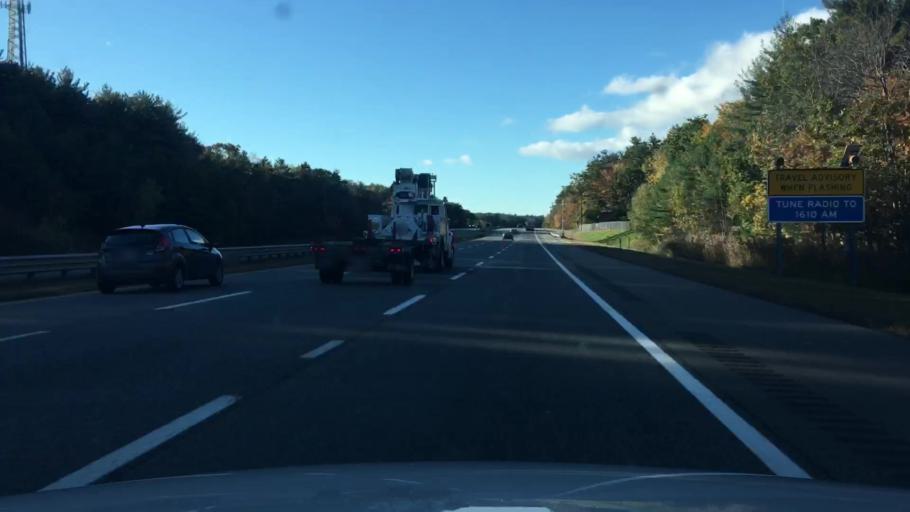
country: US
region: Maine
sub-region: York County
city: Cape Neddick
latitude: 43.1979
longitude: -70.6448
